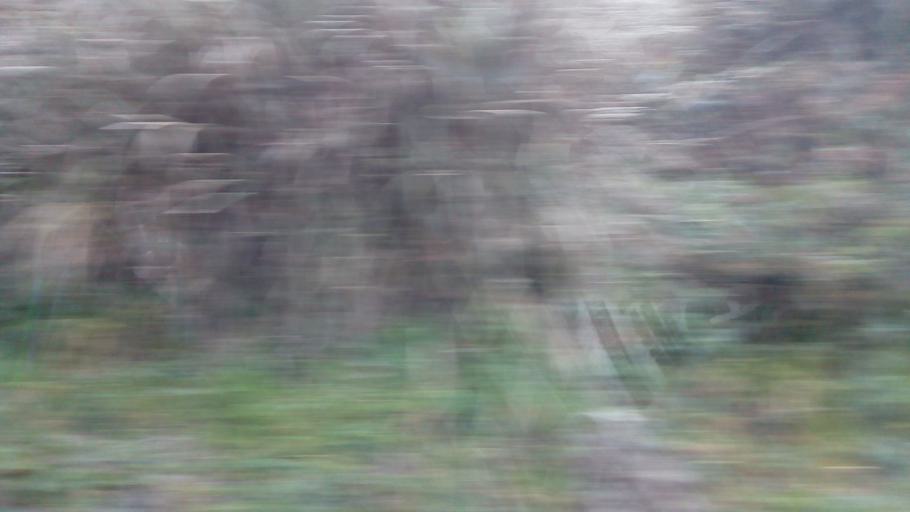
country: TW
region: Taiwan
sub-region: Hualien
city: Hualian
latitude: 24.3877
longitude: 121.3476
